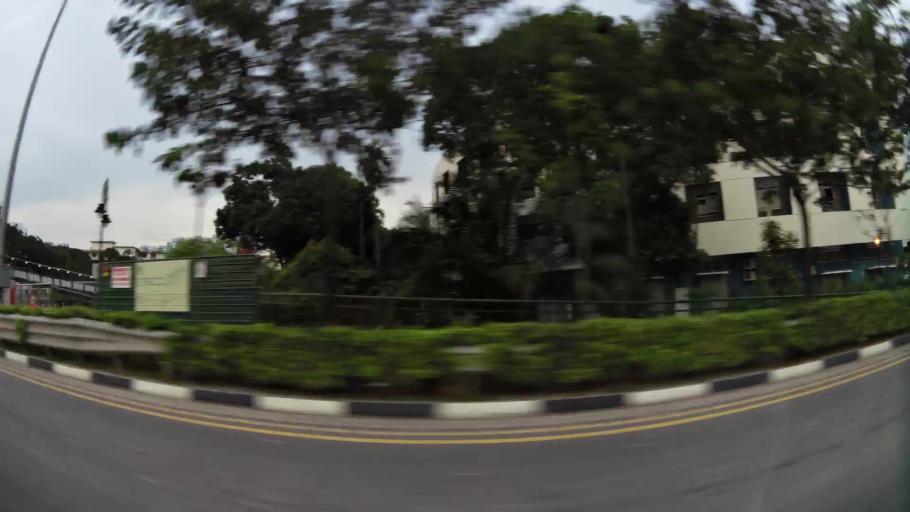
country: SG
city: Singapore
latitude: 1.3045
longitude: 103.8841
